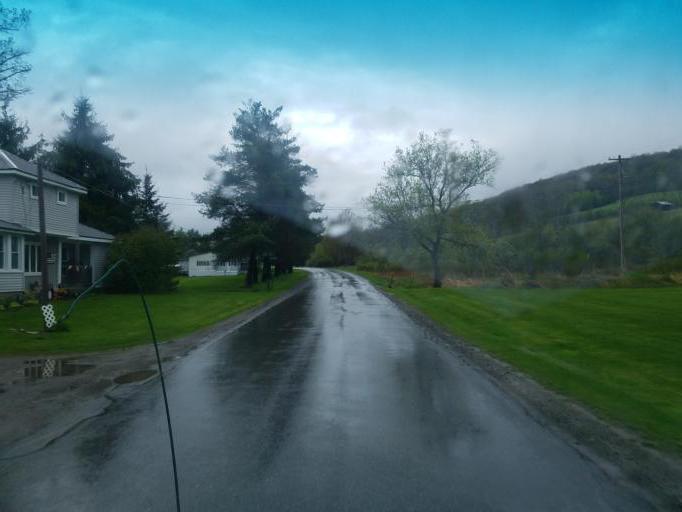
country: US
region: Pennsylvania
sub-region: Tioga County
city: Westfield
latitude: 41.9461
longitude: -77.6477
